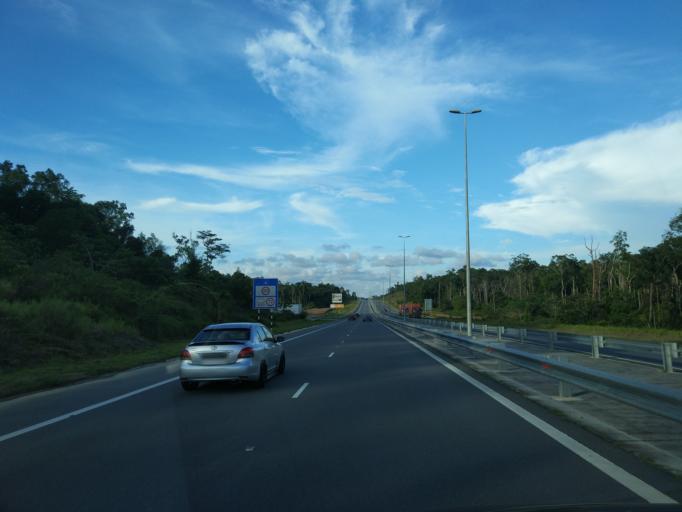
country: BN
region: Tutong
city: Tutong
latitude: 4.6776
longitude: 114.5381
